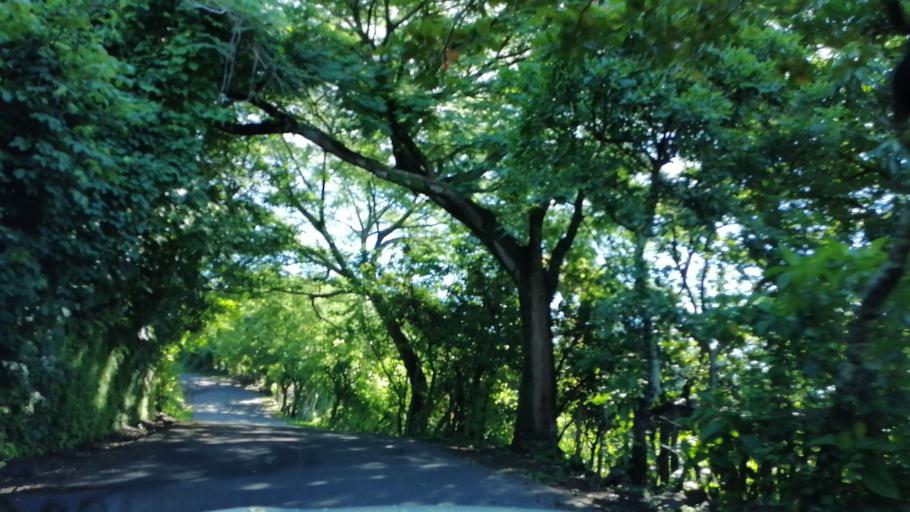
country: SV
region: Morazan
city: Cacaopera
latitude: 13.7825
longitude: -88.0341
